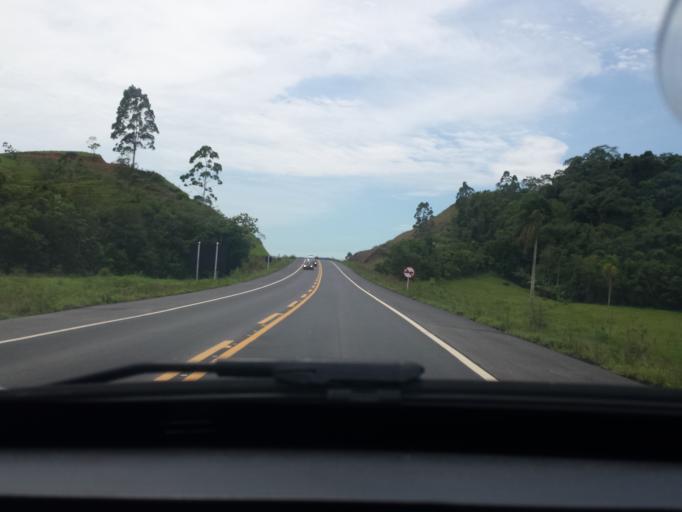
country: BR
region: Santa Catarina
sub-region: Gaspar
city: Gaspar
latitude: -26.8822
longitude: -48.8372
